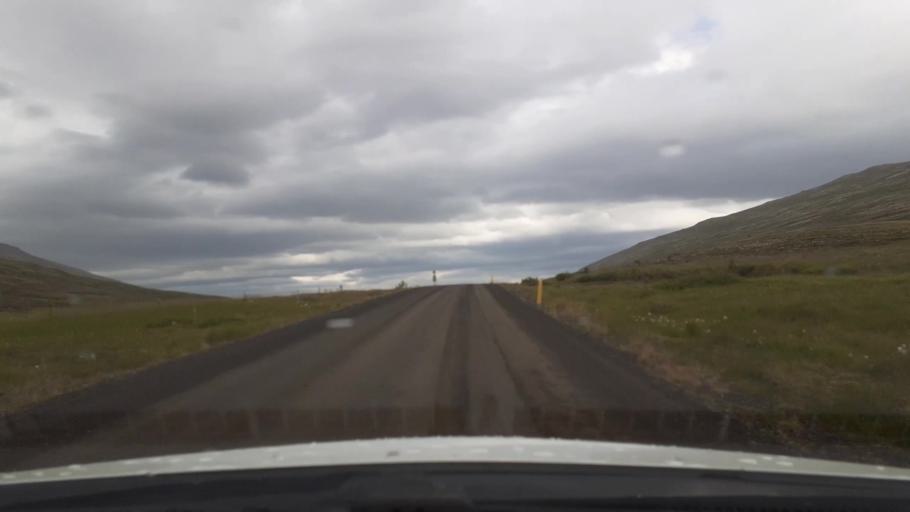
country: IS
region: Capital Region
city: Mosfellsbaer
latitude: 64.4875
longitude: -21.5180
